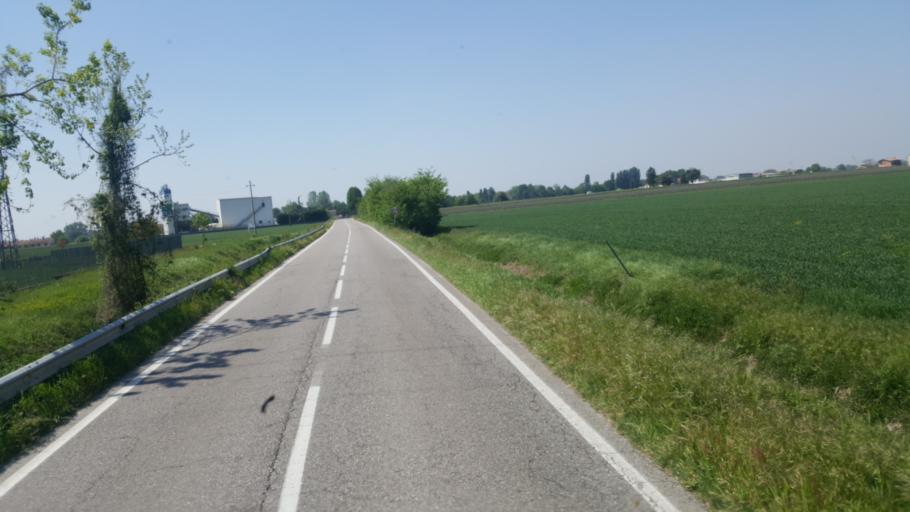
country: IT
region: Lombardy
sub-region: Provincia di Mantova
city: Quistello
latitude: 45.0134
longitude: 10.9564
